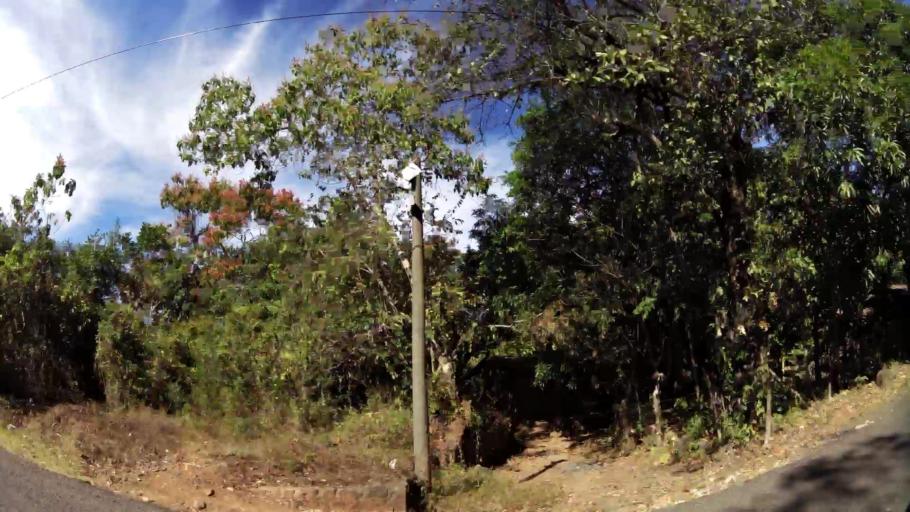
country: SV
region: Cuscatlan
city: Suchitoto
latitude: 13.9299
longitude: -89.0457
